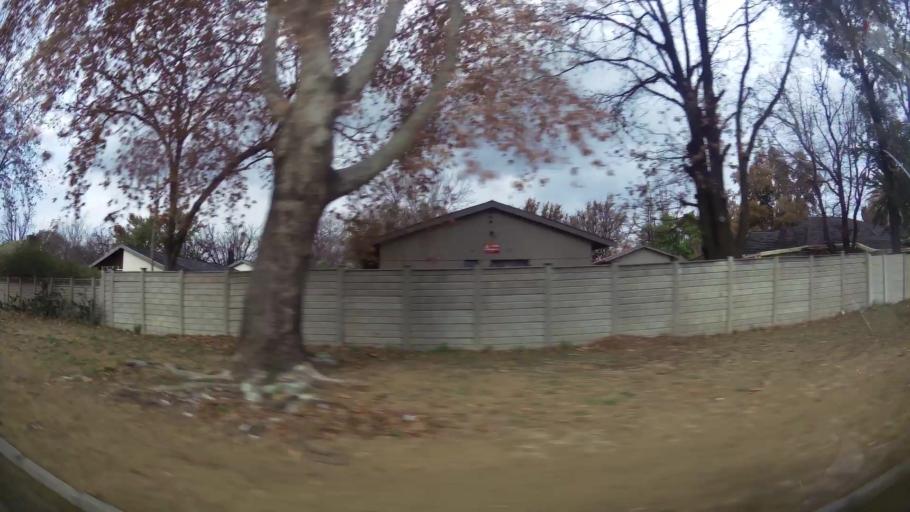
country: ZA
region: Orange Free State
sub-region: Fezile Dabi District Municipality
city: Sasolburg
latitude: -26.8099
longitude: 27.8280
